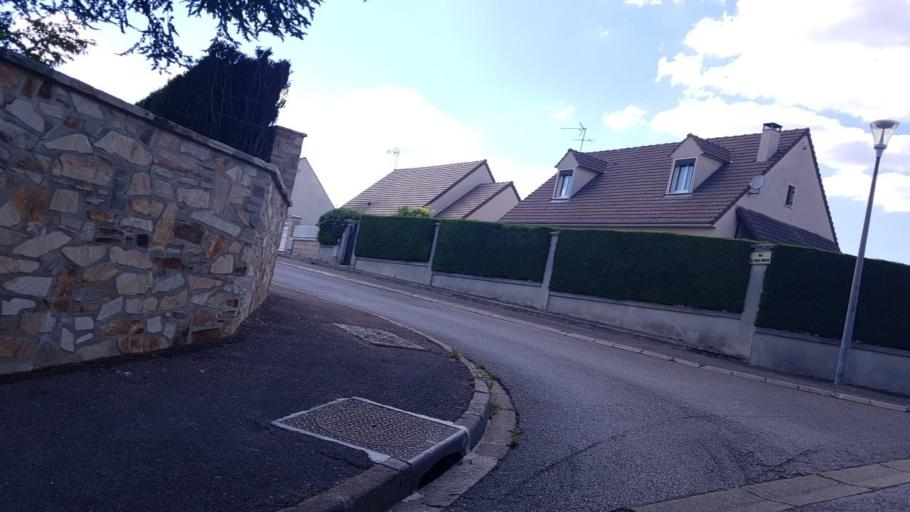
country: FR
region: Picardie
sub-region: Departement de l'Oise
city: Ver-sur-Launette
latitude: 49.1064
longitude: 2.6829
